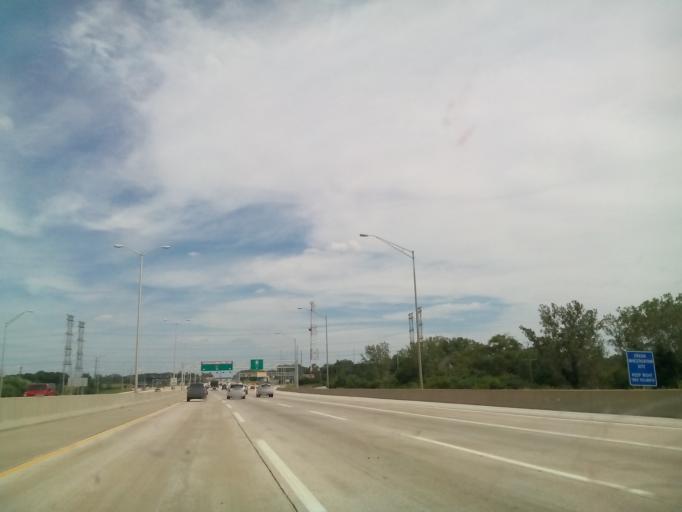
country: US
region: Illinois
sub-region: Kane County
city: North Aurora
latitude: 41.7963
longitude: -88.3157
